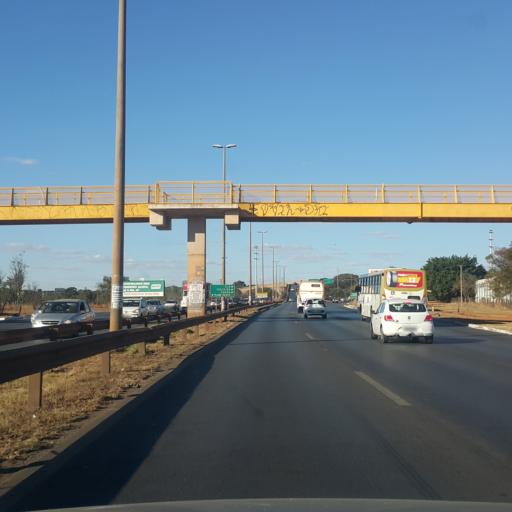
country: BR
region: Federal District
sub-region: Brasilia
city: Brasilia
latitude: -15.7872
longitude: -47.9459
